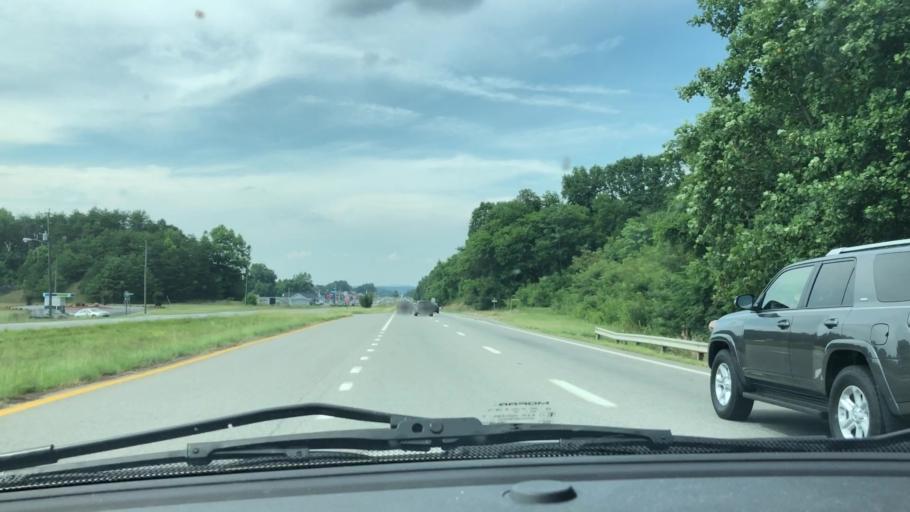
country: US
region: Virginia
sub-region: Henry County
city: Chatmoss
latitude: 36.5926
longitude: -79.8626
